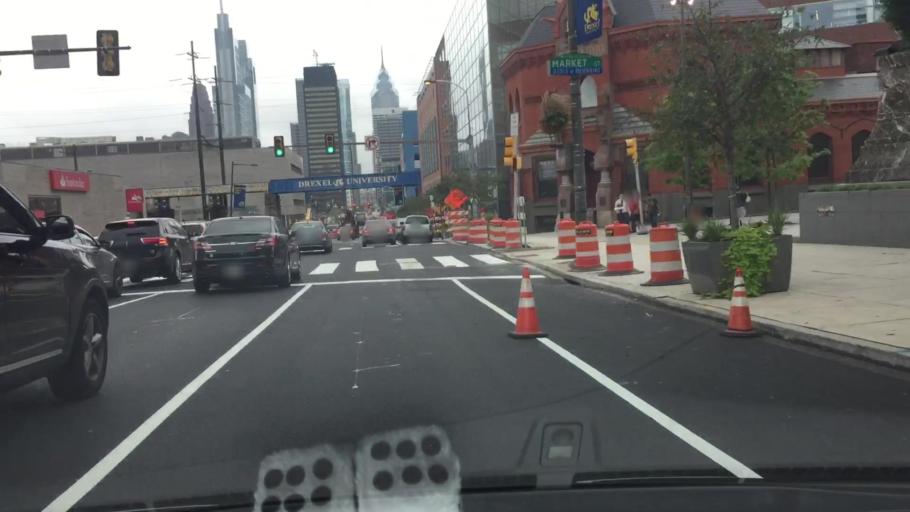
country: US
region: Pennsylvania
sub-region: Philadelphia County
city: Philadelphia
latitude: 39.9553
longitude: -75.1876
